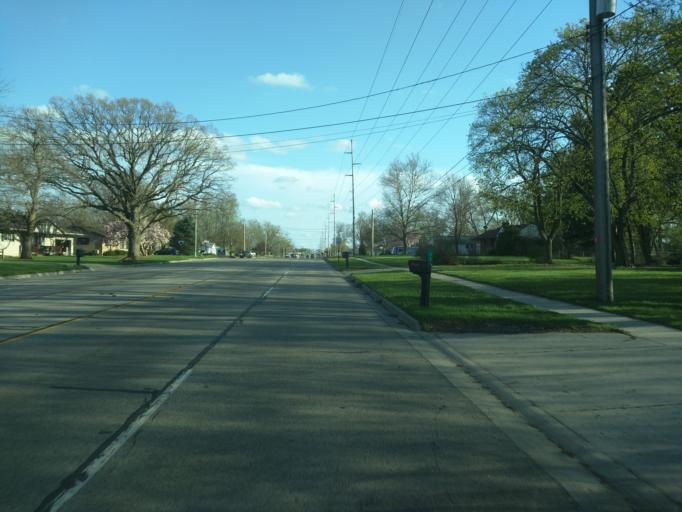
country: US
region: Michigan
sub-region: Eaton County
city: Waverly
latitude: 42.7369
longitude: -84.6424
